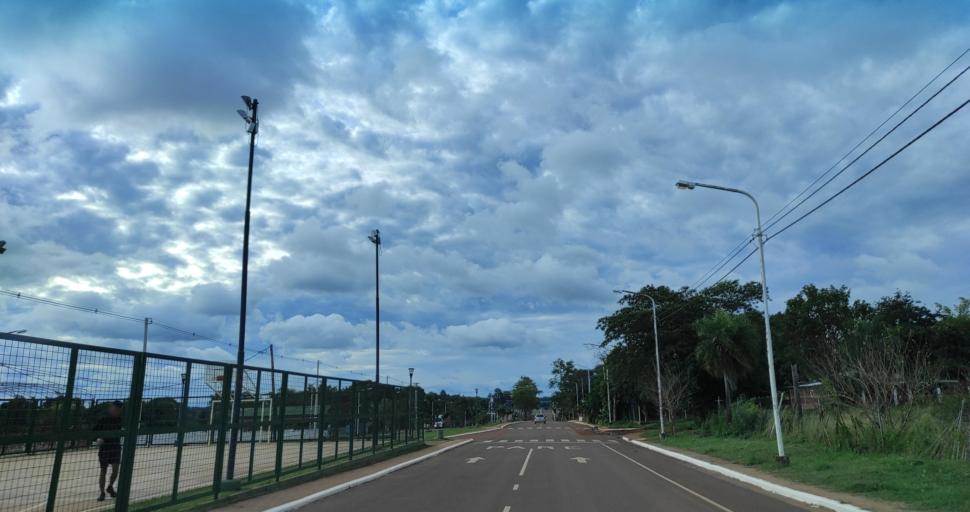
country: AR
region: Misiones
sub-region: Departamento de Candelaria
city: Candelaria
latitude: -27.4579
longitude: -55.7442
